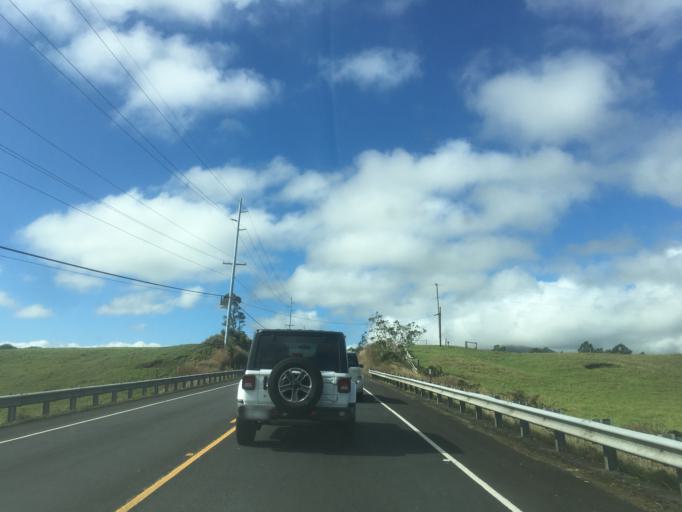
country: US
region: Hawaii
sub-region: Hawaii County
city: Waimea
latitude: 20.0479
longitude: -155.5781
